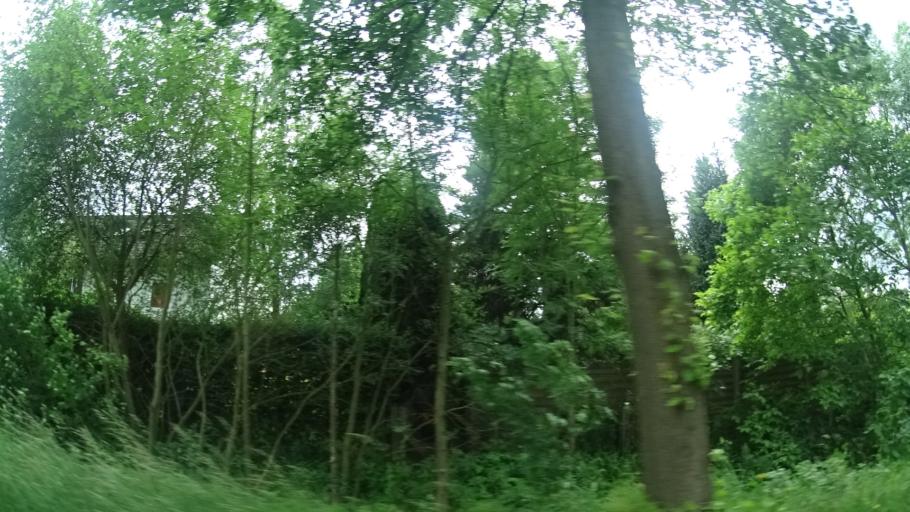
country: DE
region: Lower Saxony
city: Bad Munder am Deister
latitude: 52.1931
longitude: 9.4660
